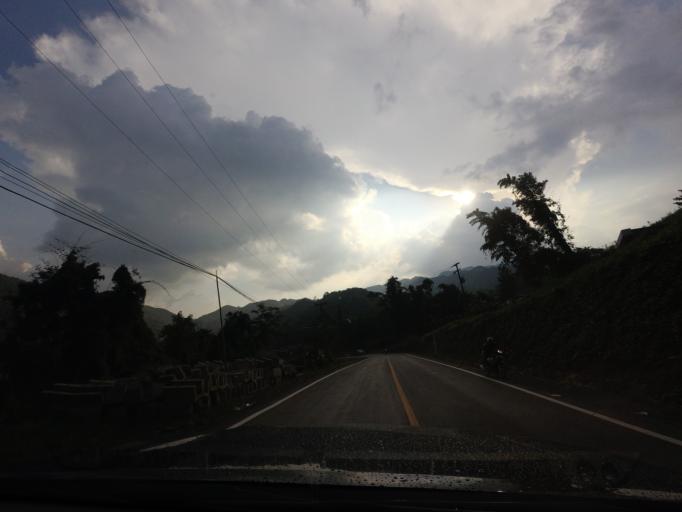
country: TH
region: Nan
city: Bo Kluea
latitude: 19.2040
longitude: 101.1857
